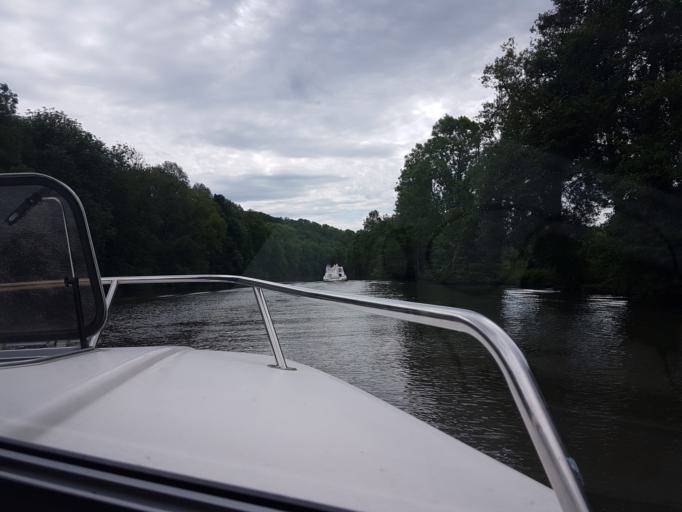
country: FR
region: Bourgogne
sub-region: Departement de la Nievre
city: Clamecy
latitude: 47.4704
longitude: 3.5280
